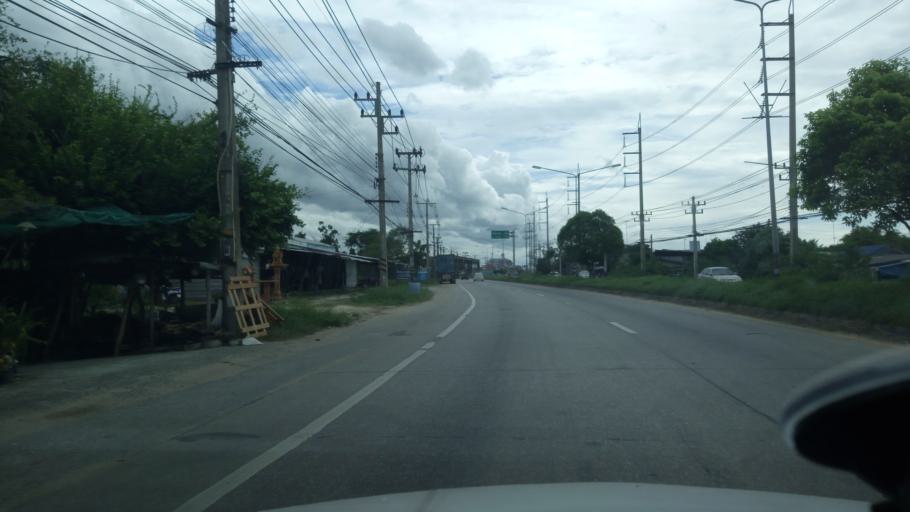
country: TH
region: Chon Buri
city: Phanat Nikhom
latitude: 13.4430
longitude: 101.1511
